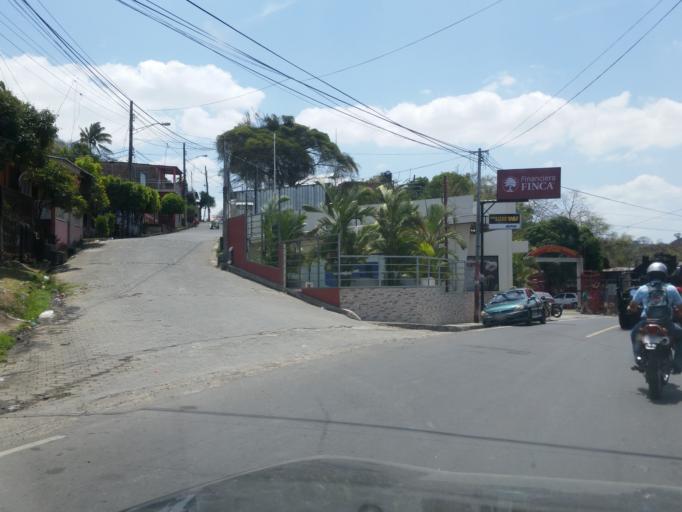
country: NI
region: Boaco
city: Boaco
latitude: 12.4666
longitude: -85.6589
